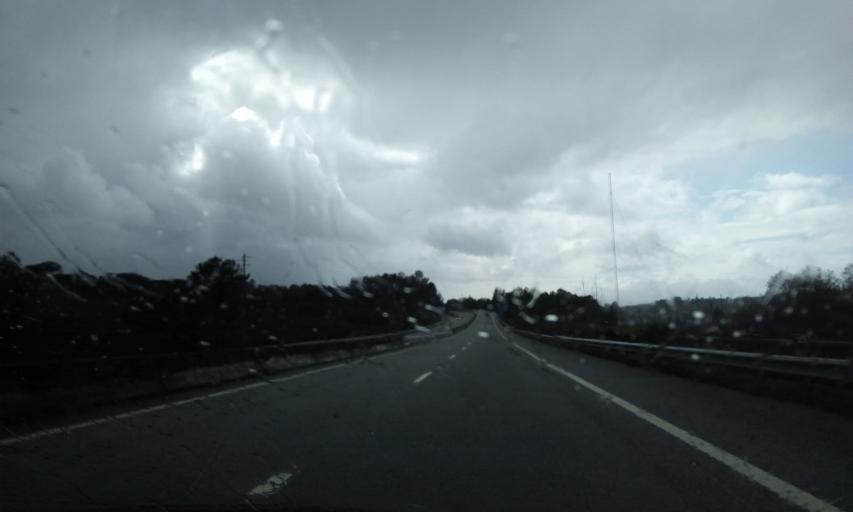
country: PT
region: Viseu
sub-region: Viseu
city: Viseu
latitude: 40.6289
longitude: -7.8945
